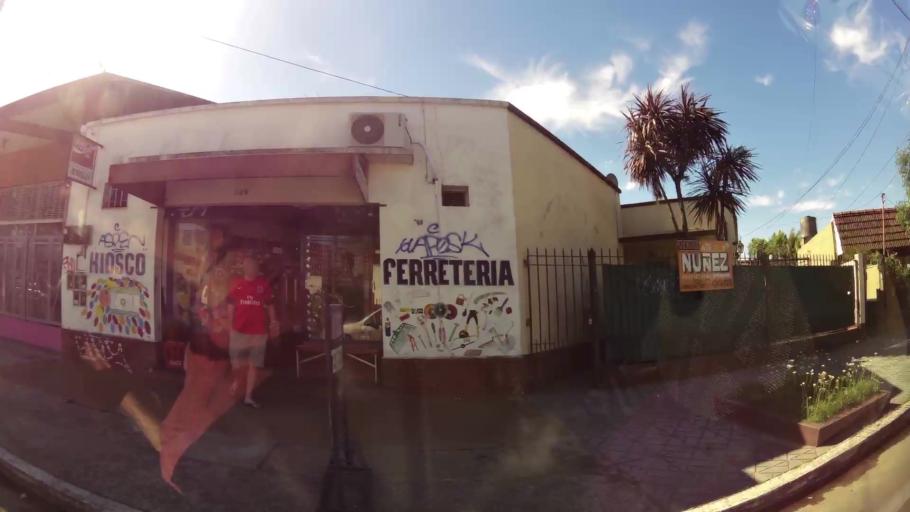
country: AR
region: Buenos Aires
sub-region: Partido de Lomas de Zamora
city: Lomas de Zamora
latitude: -34.7678
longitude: -58.4093
